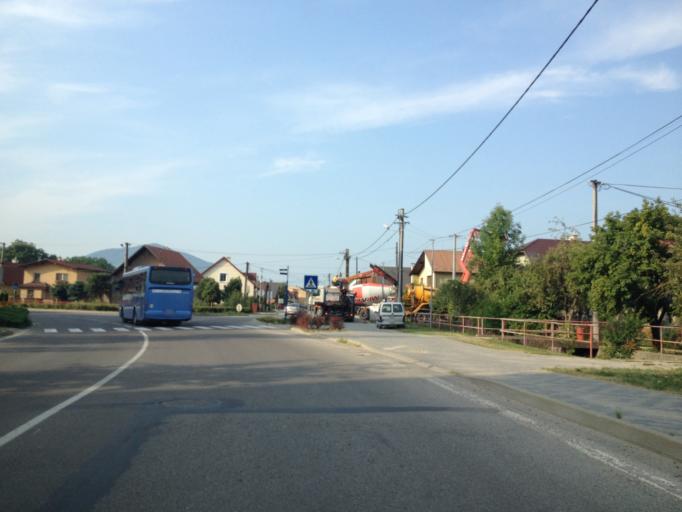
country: SK
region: Nitriansky
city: Puchov
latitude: 49.0611
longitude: 18.3226
